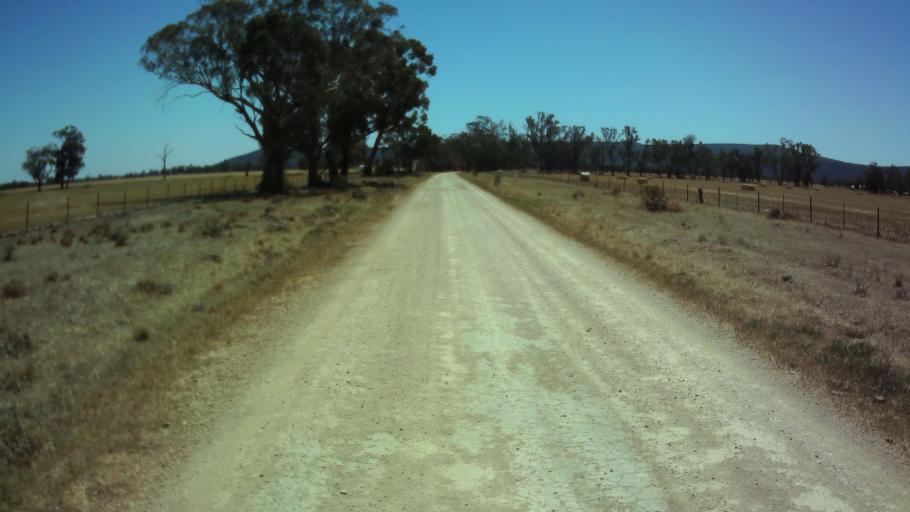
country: AU
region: New South Wales
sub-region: Weddin
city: Grenfell
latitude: -34.0235
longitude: 147.9617
